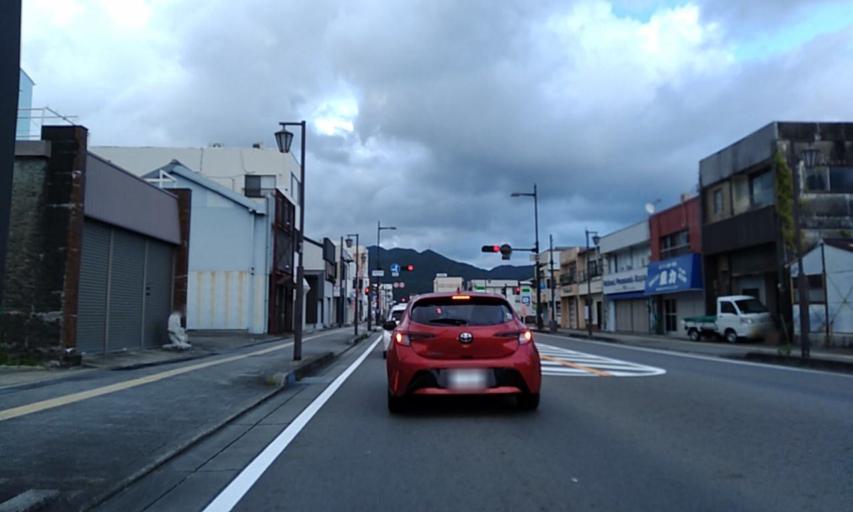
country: JP
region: Wakayama
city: Shingu
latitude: 33.7239
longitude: 135.9866
